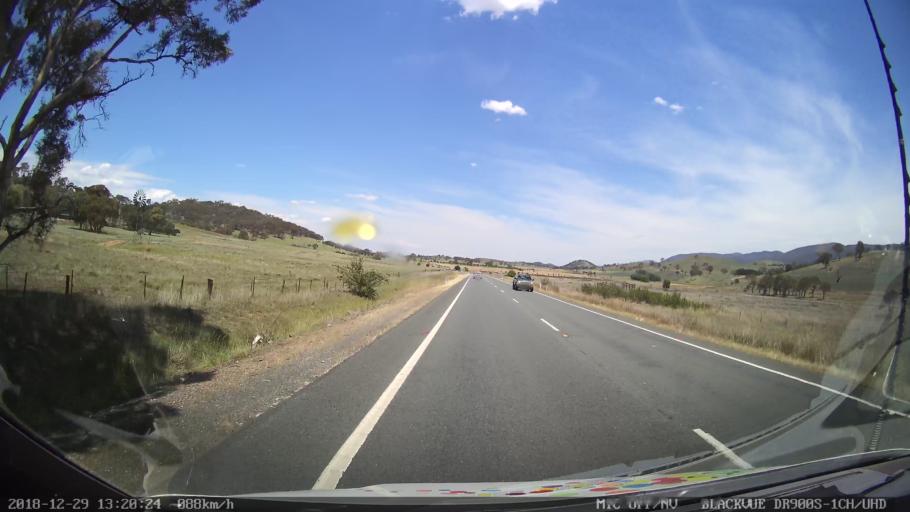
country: AU
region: Australian Capital Territory
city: Macarthur
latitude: -35.7783
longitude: 149.1619
